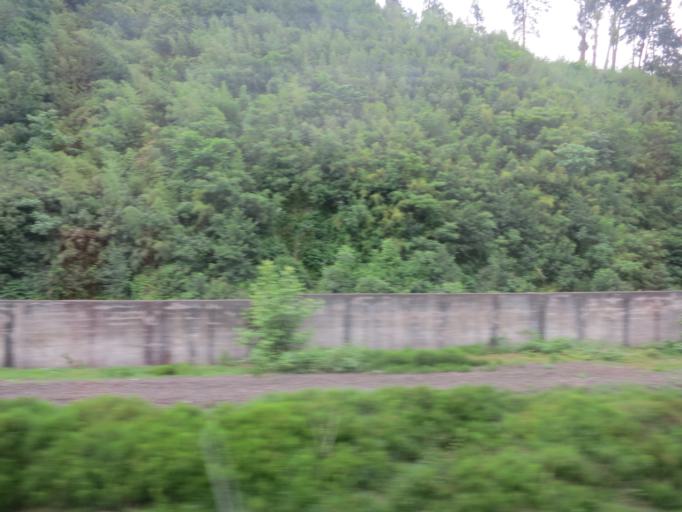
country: GE
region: Ajaria
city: Kobuleti
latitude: 41.7722
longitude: 41.7567
